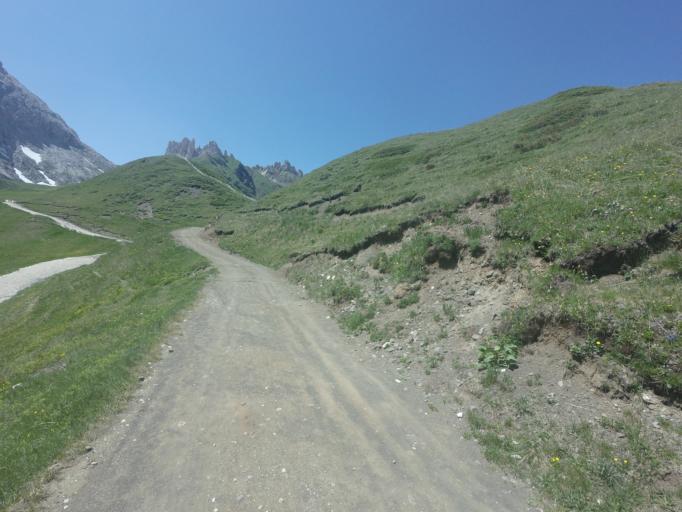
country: IT
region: Trentino-Alto Adige
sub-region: Provincia di Trento
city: Mazzin
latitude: 46.4973
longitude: 11.6546
